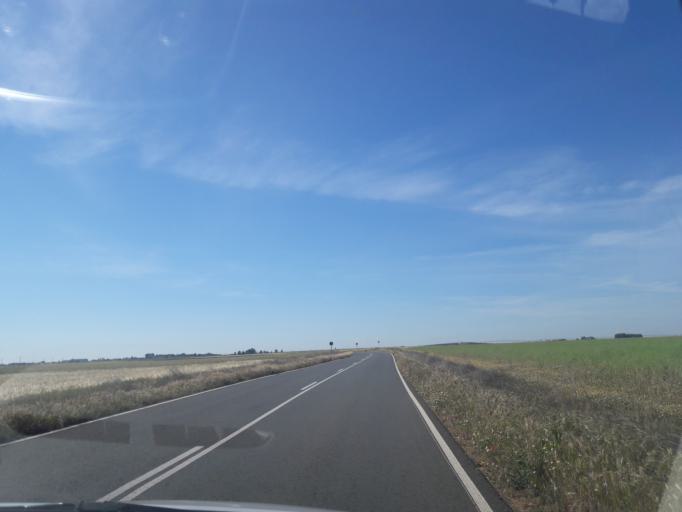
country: ES
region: Castille and Leon
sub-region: Provincia de Salamanca
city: Espino de la Orbada
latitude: 41.0972
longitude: -5.4174
